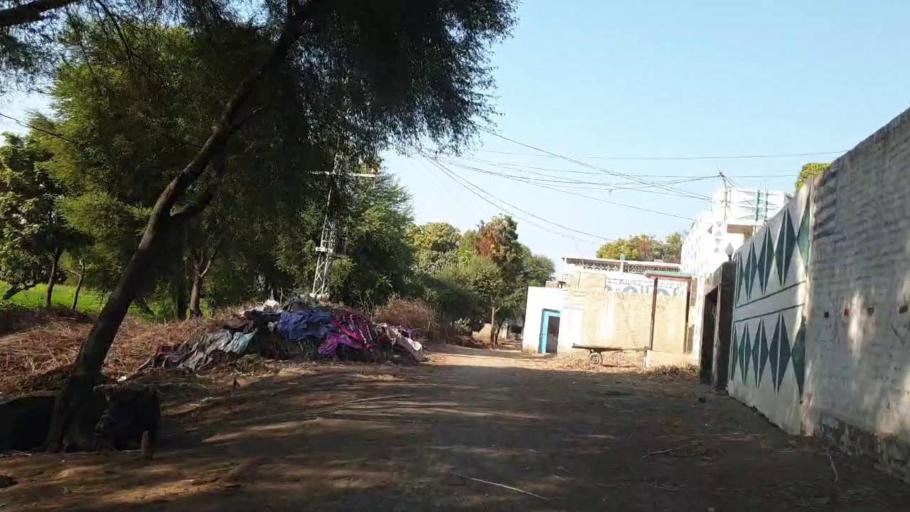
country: PK
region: Sindh
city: Tando Jam
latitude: 25.5087
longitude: 68.5365
